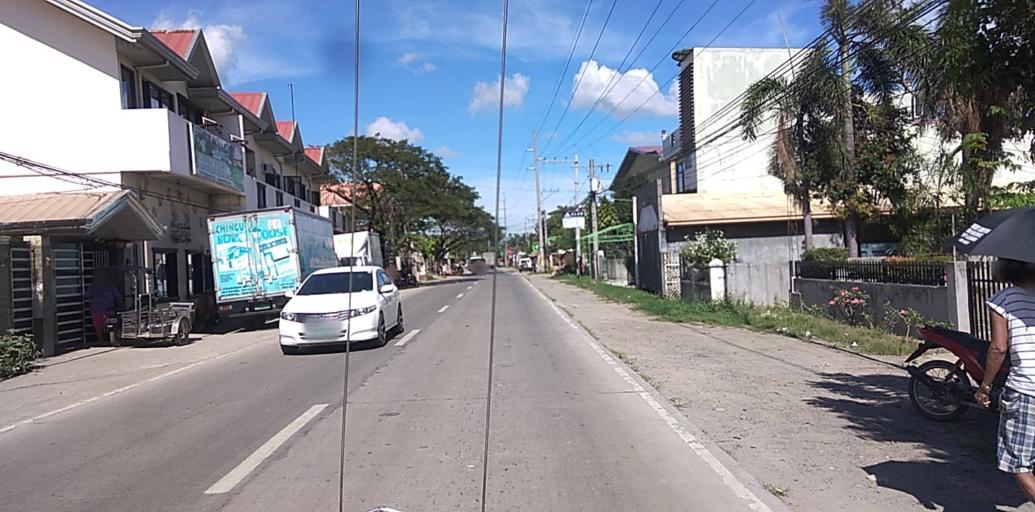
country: PH
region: Central Luzon
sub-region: Province of Pampanga
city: Arayat
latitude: 15.1248
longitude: 120.7758
